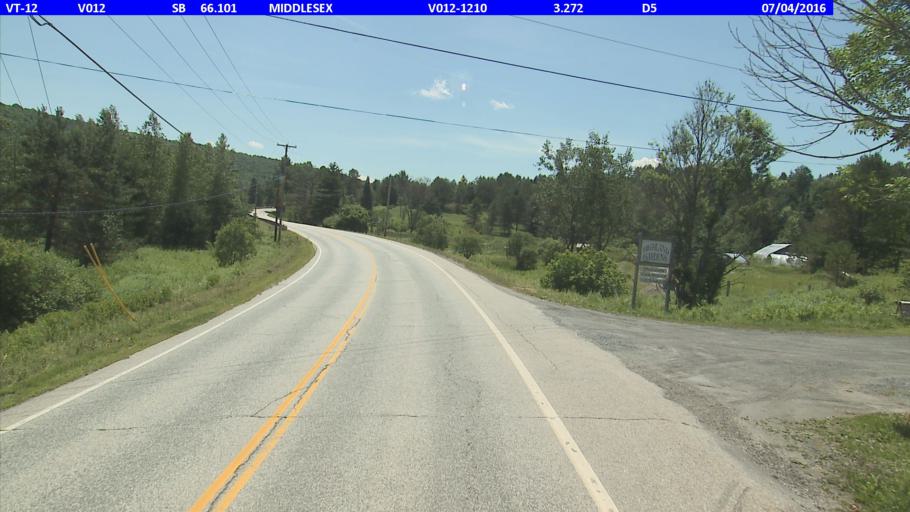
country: US
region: Vermont
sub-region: Washington County
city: Montpelier
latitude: 44.3474
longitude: -72.5661
